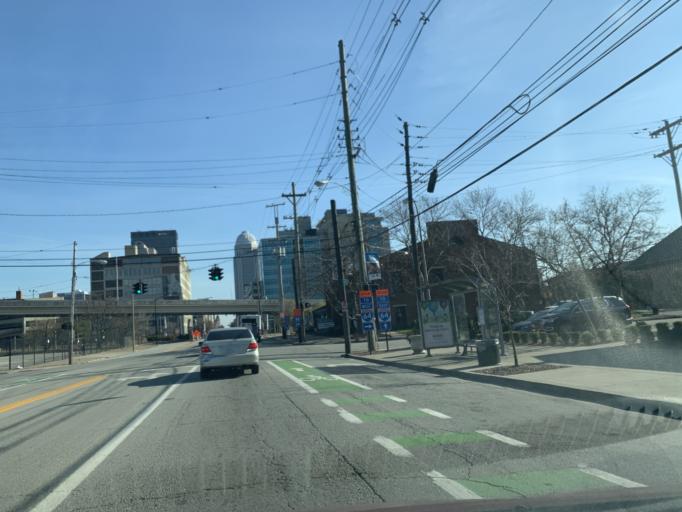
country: US
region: Kentucky
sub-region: Jefferson County
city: Louisville
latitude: 38.2563
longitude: -85.7672
